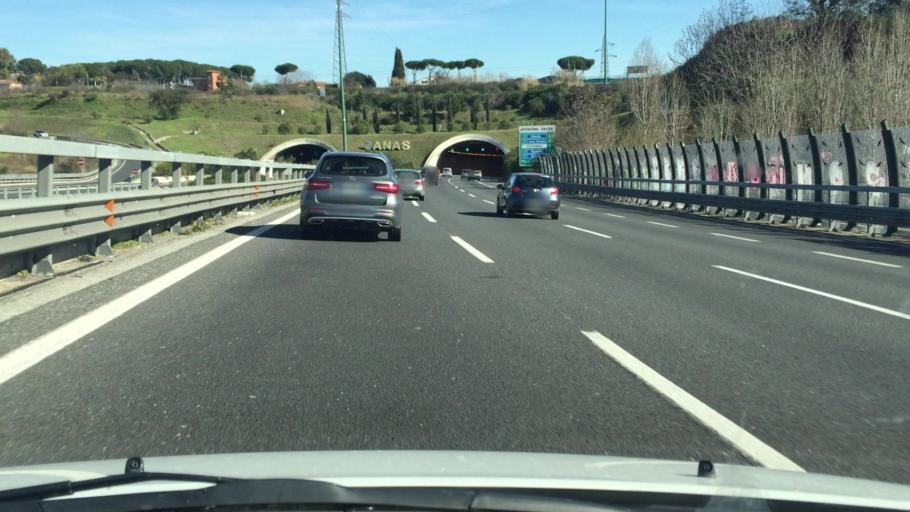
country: VA
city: Vatican City
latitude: 41.9692
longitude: 12.4050
